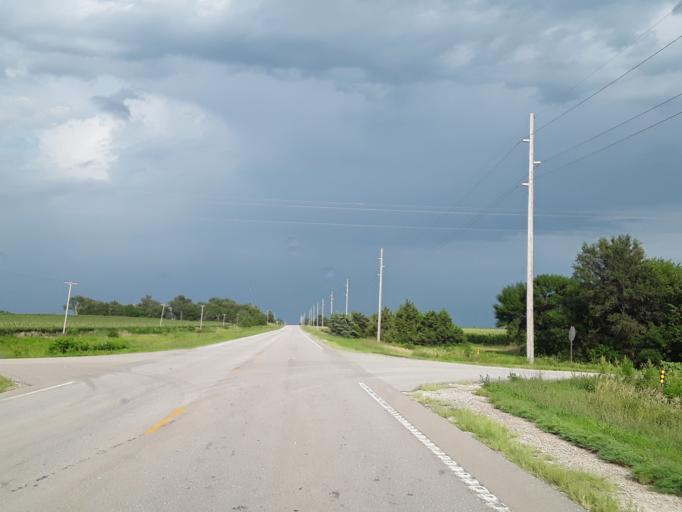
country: US
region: Nebraska
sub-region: Saunders County
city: Ashland
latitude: 41.0887
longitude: -96.4072
